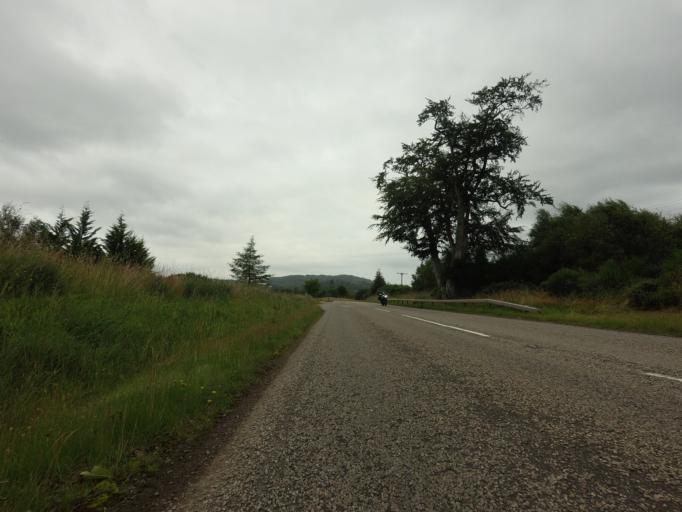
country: GB
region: Scotland
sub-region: Highland
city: Evanton
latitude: 57.9175
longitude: -4.3937
